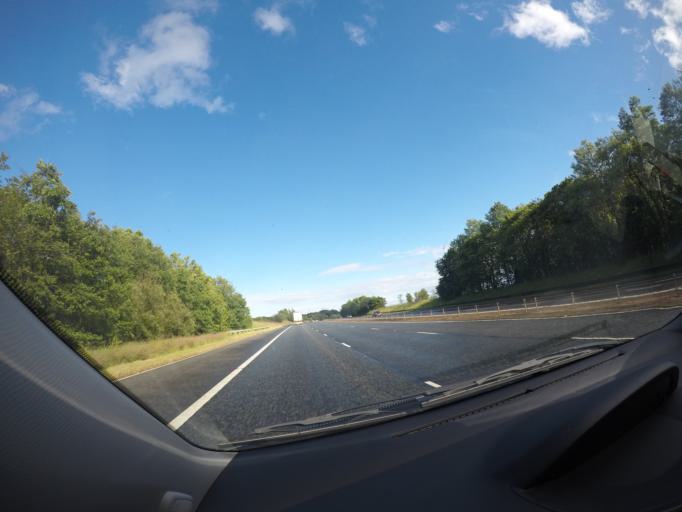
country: GB
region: Scotland
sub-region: Dumfries and Galloway
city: Annan
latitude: 55.0431
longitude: -3.1844
